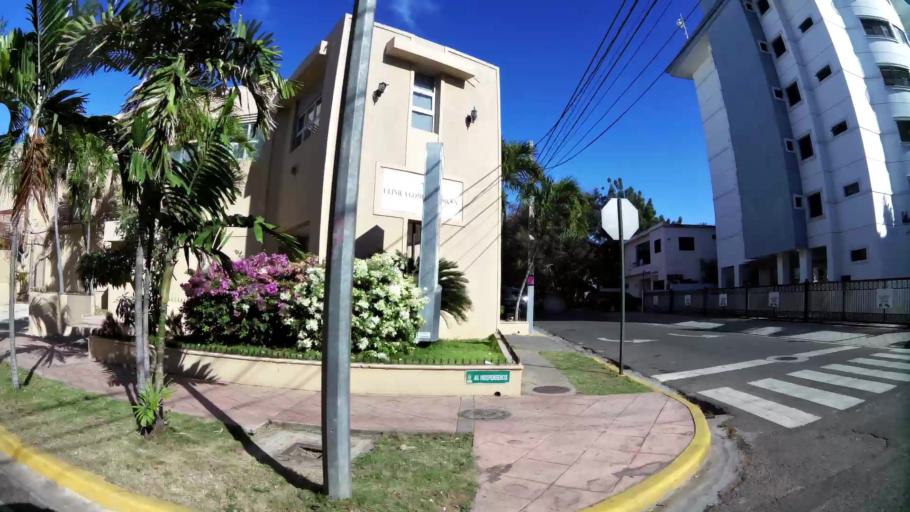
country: DO
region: Nacional
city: Ciudad Nueva
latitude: 18.4614
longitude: -69.9063
